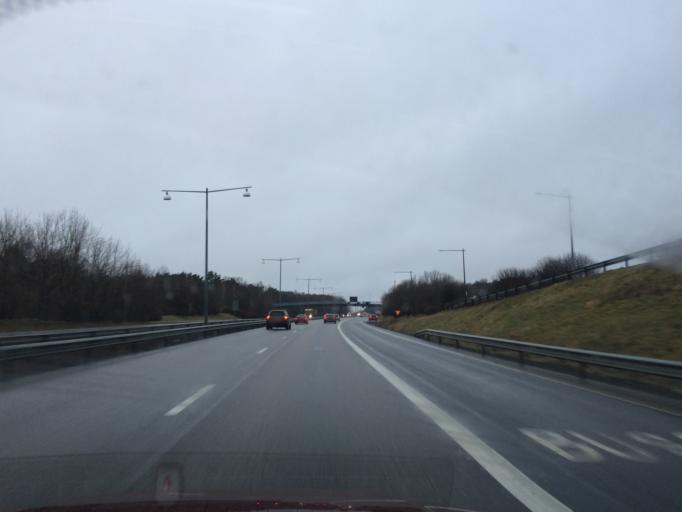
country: SE
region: Vaestra Goetaland
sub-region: Goteborg
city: Majorna
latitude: 57.6616
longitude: 11.8917
